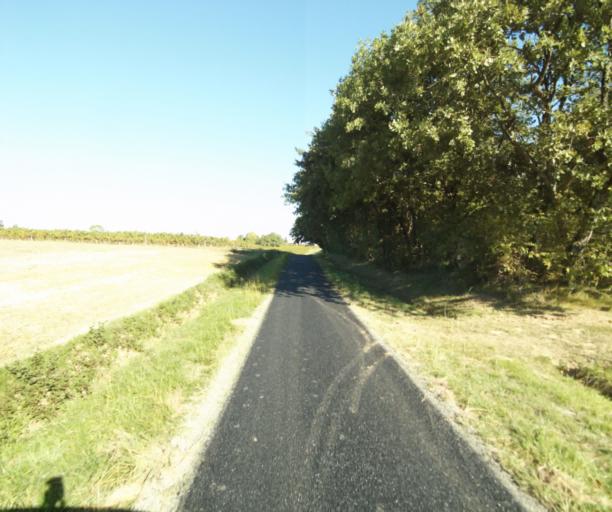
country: FR
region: Midi-Pyrenees
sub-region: Departement du Gers
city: Gondrin
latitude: 43.8117
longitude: 0.1953
